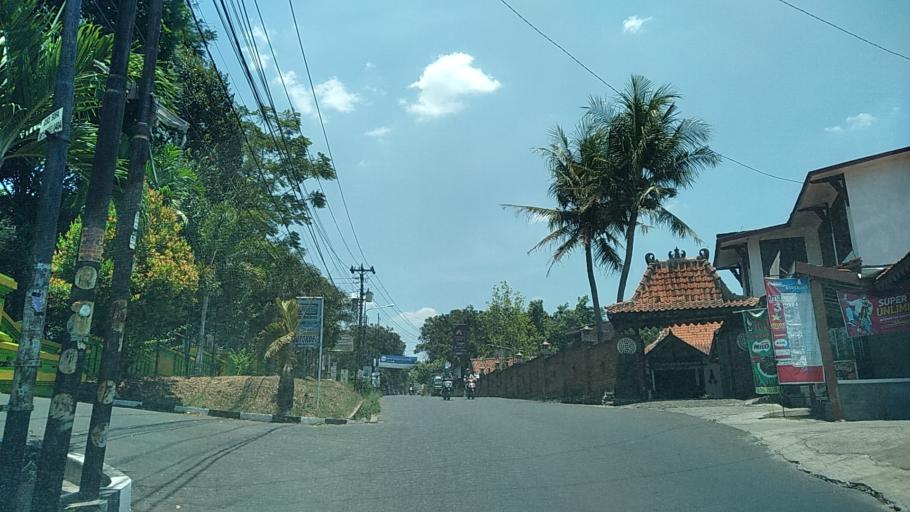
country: ID
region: Central Java
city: Ungaran
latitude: -7.0777
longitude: 110.4214
